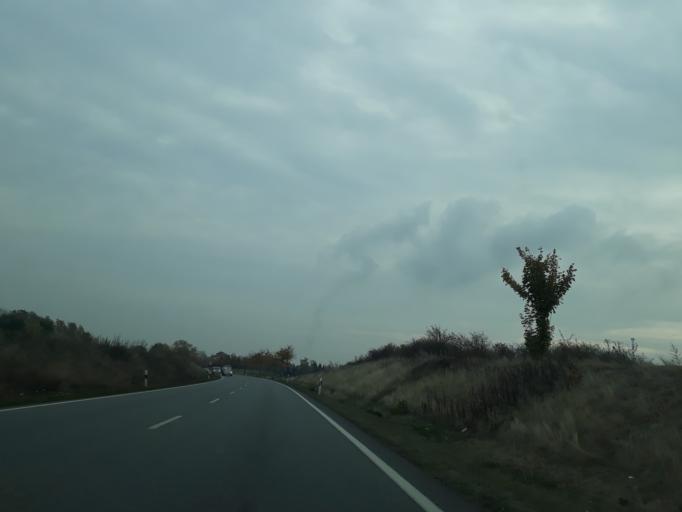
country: DE
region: Saxony
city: Moritzburg
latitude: 51.1354
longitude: 13.6886
